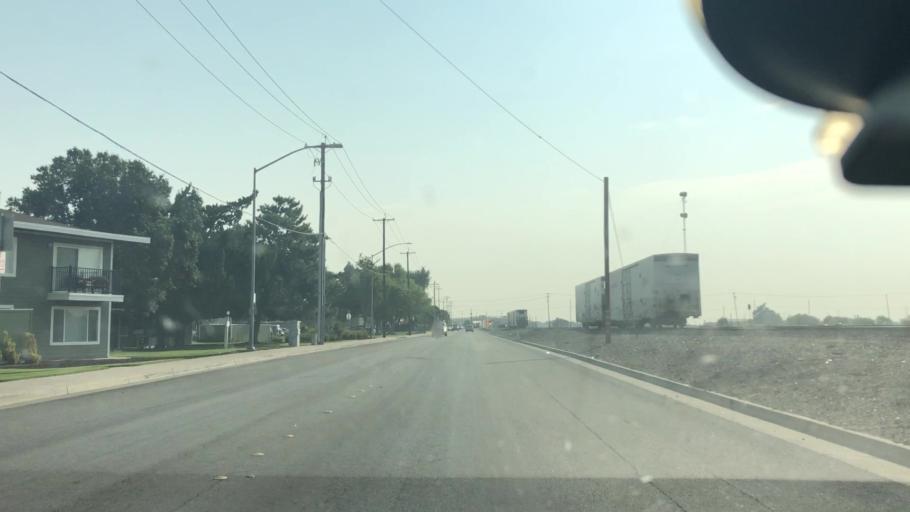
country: US
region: California
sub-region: San Joaquin County
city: Tracy
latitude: 37.7358
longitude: -121.4208
